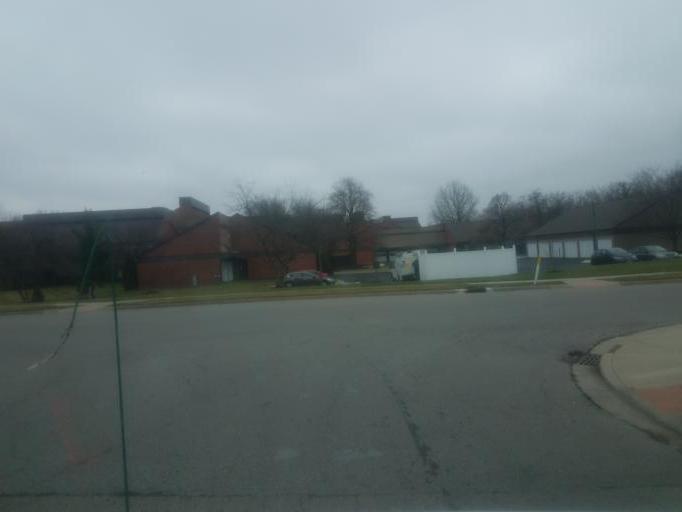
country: US
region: Ohio
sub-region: Franklin County
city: Minerva Park
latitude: 40.0904
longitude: -82.9400
